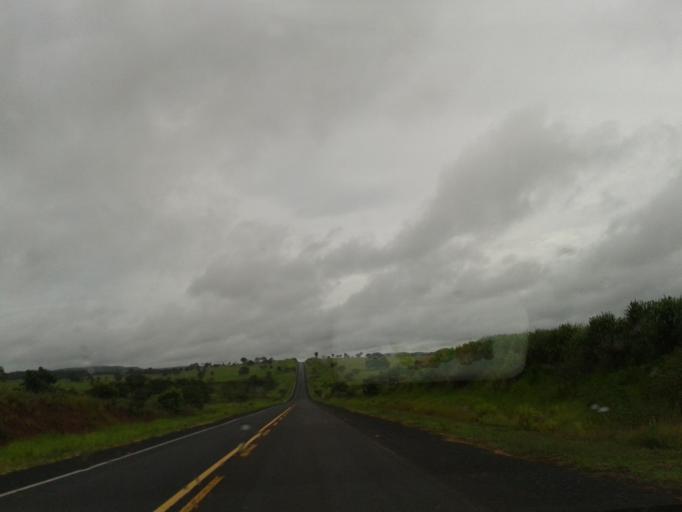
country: BR
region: Minas Gerais
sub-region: Santa Vitoria
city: Santa Vitoria
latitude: -19.2700
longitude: -50.0054
